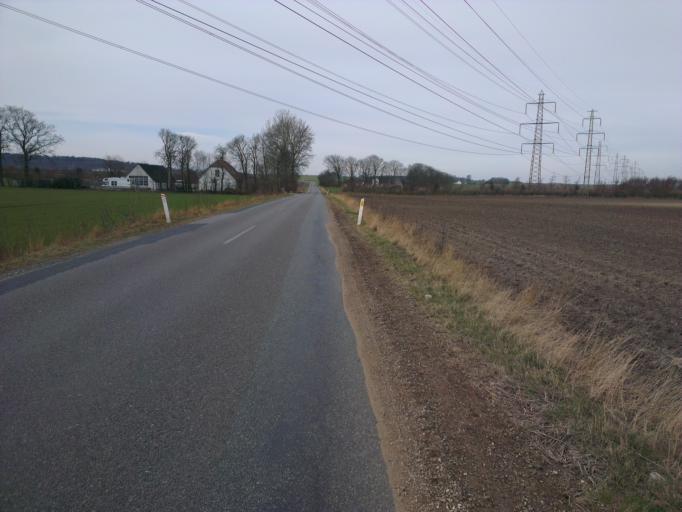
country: DK
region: Capital Region
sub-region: Frederikssund Kommune
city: Skibby
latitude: 55.8028
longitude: 11.9721
